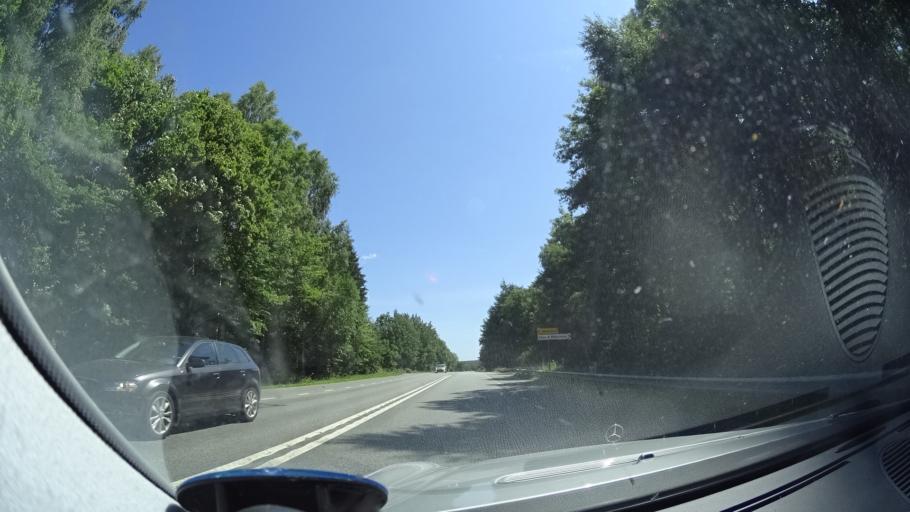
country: SE
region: Skane
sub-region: Kristianstads Kommun
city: Onnestad
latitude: 55.9335
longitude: 13.9209
